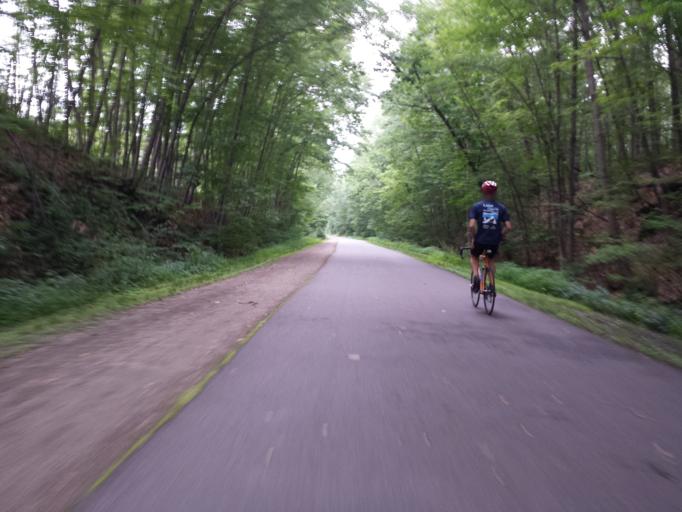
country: US
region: New York
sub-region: Dutchess County
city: Myers Corner
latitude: 41.6156
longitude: -73.8453
